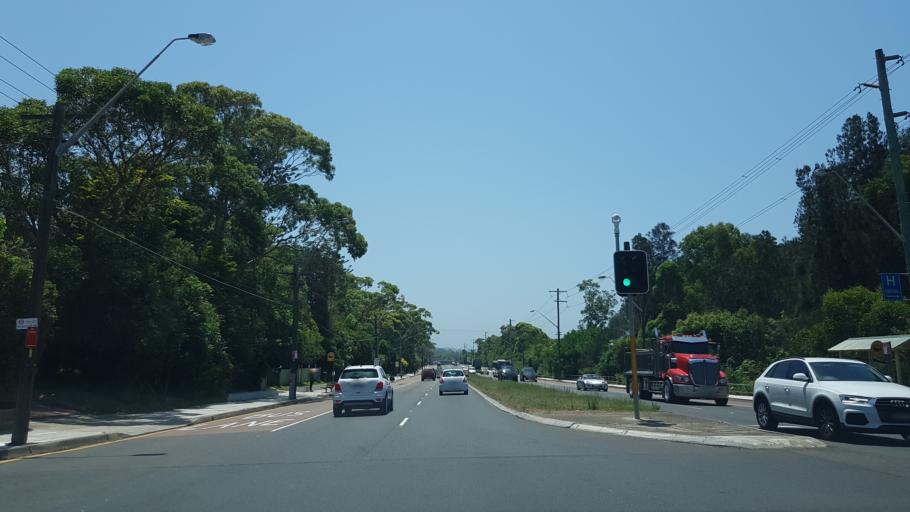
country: AU
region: New South Wales
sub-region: Pittwater
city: Warriewood
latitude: -33.6878
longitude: 151.3046
